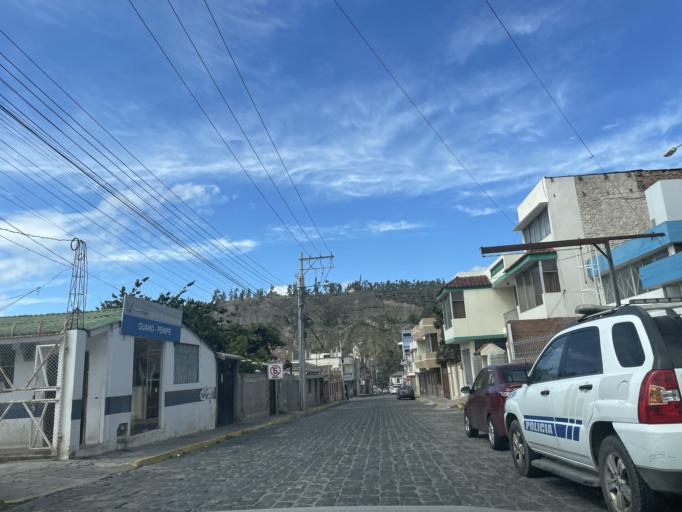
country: EC
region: Chimborazo
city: Guano
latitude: -1.6059
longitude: -78.6444
